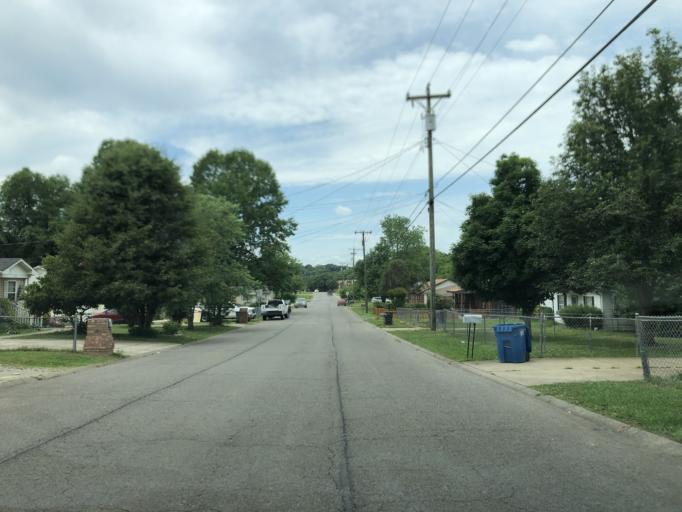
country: US
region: Tennessee
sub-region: Davidson County
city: Nashville
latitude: 36.2457
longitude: -86.7738
